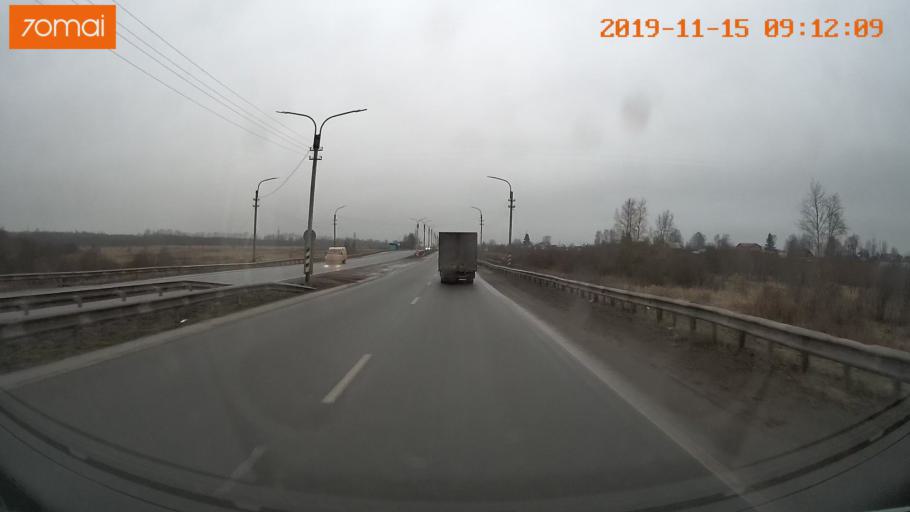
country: RU
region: Vologda
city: Tonshalovo
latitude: 59.2049
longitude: 37.9400
